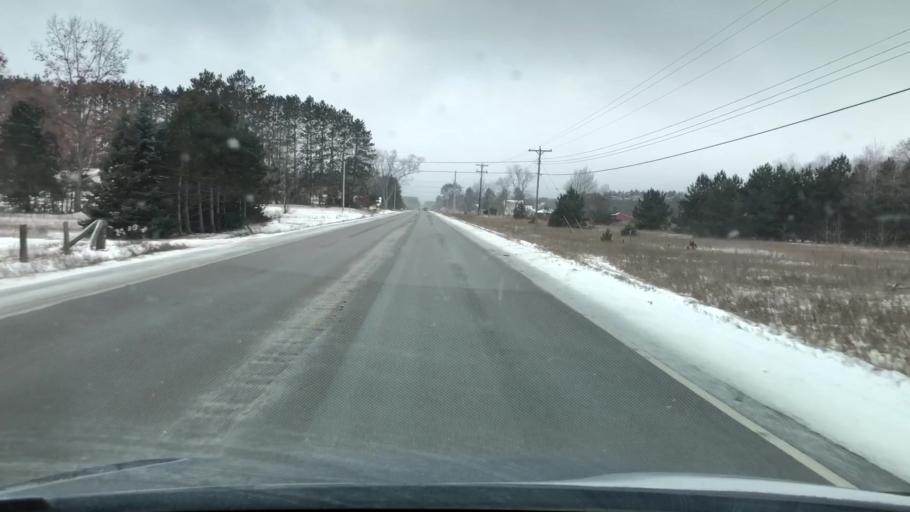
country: US
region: Michigan
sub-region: Wexford County
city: Cadillac
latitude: 44.2813
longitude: -85.4399
